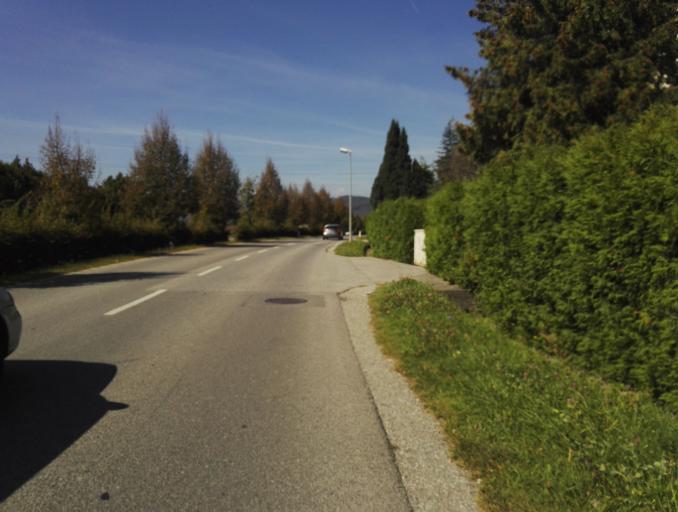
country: AT
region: Styria
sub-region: Politischer Bezirk Graz-Umgebung
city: Gratkorn
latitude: 47.1237
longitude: 15.3543
